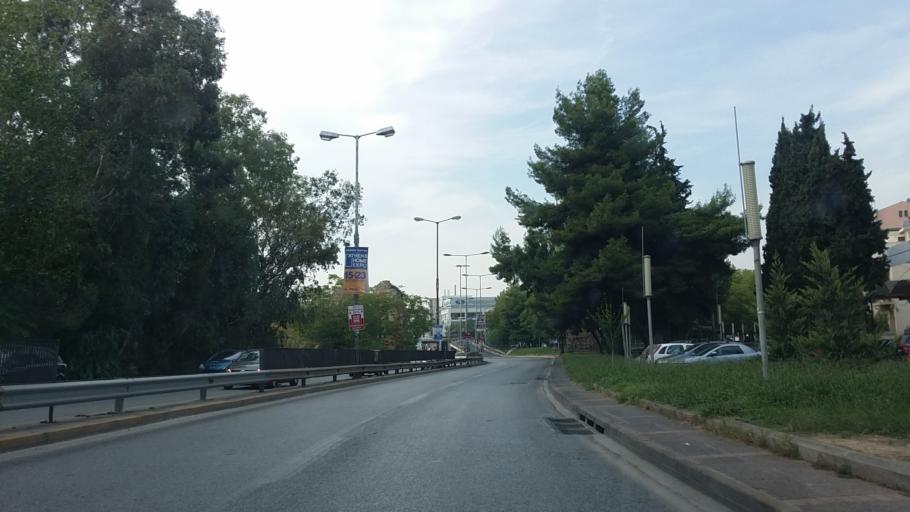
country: GR
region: Attica
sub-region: Nomarchia Athinas
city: Filothei
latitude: 38.0331
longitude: 23.7738
